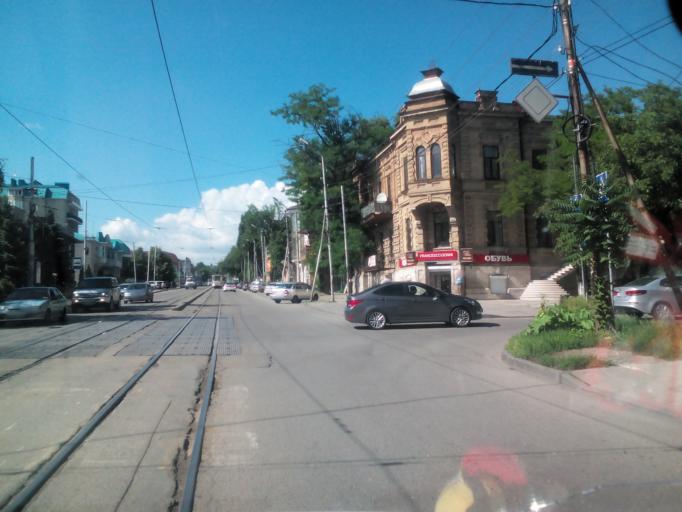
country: RU
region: Stavropol'skiy
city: Pyatigorsk
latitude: 44.0388
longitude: 43.0645
